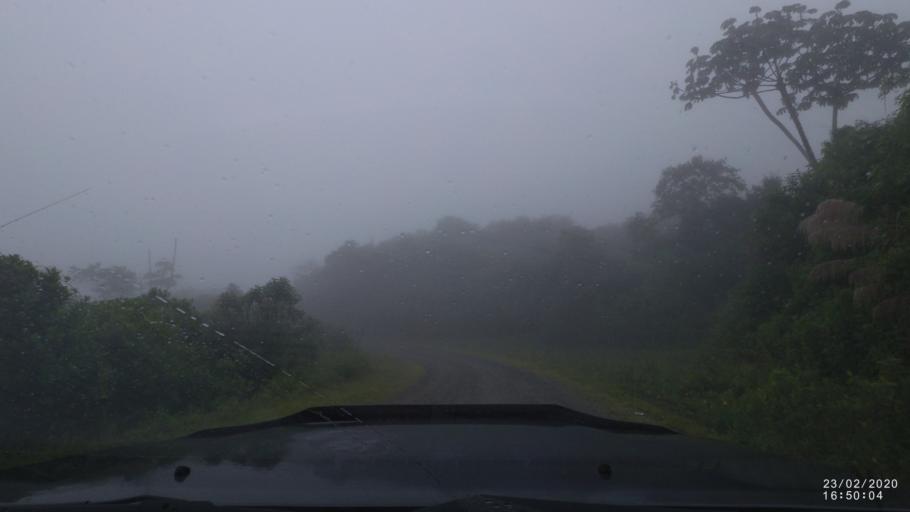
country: BO
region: Cochabamba
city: Colomi
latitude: -17.0917
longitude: -65.9874
